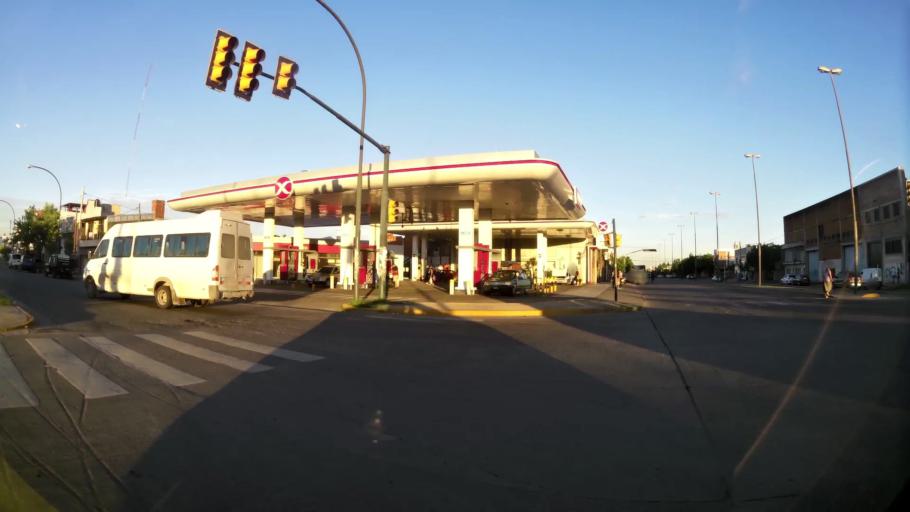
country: AR
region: Santa Fe
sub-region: Departamento de Rosario
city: Rosario
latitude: -32.9717
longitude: -60.6874
